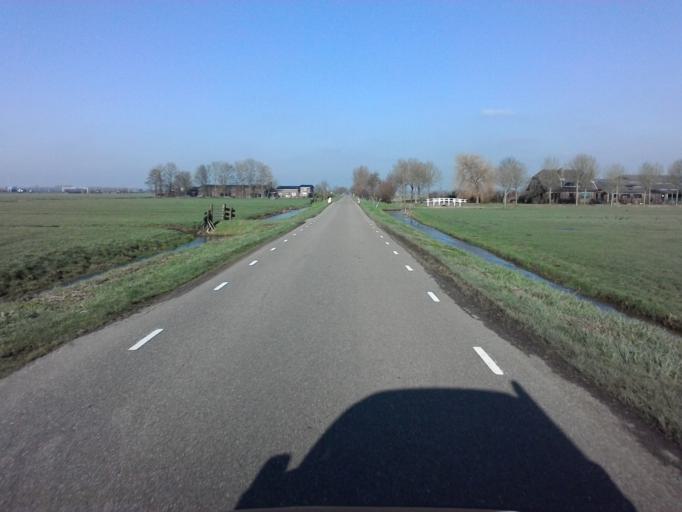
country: NL
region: South Holland
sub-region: Gemeente Gorinchem
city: Gorinchem
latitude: 51.8835
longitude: 4.9794
